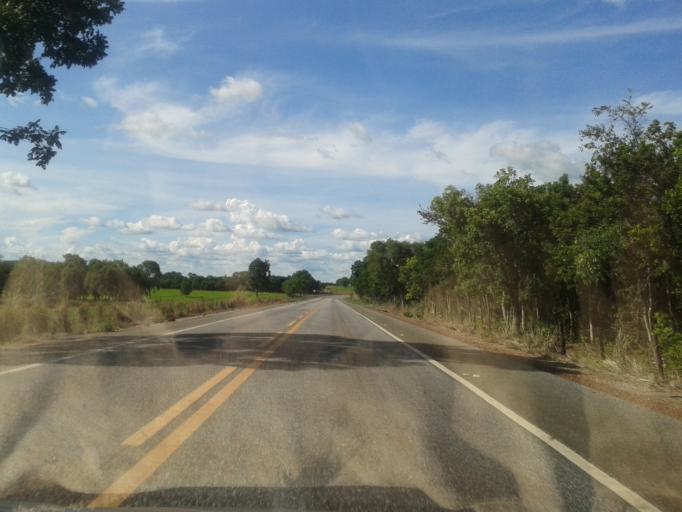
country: BR
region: Goias
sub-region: Mozarlandia
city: Mozarlandia
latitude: -14.8844
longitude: -50.5523
